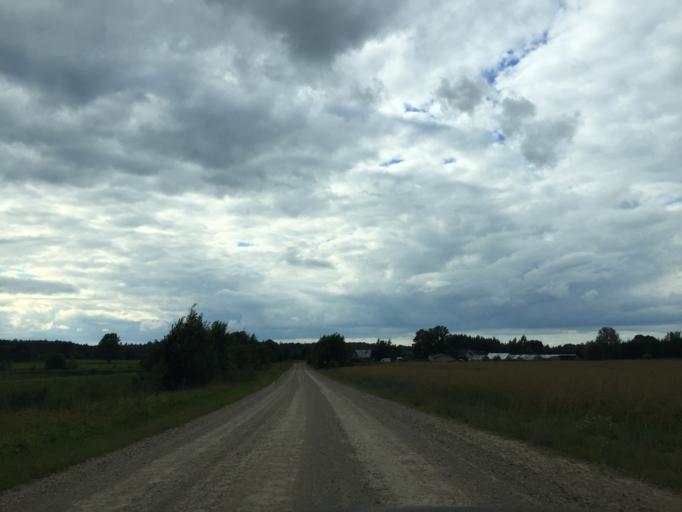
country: LV
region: Malpils
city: Malpils
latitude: 56.9495
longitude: 24.9932
